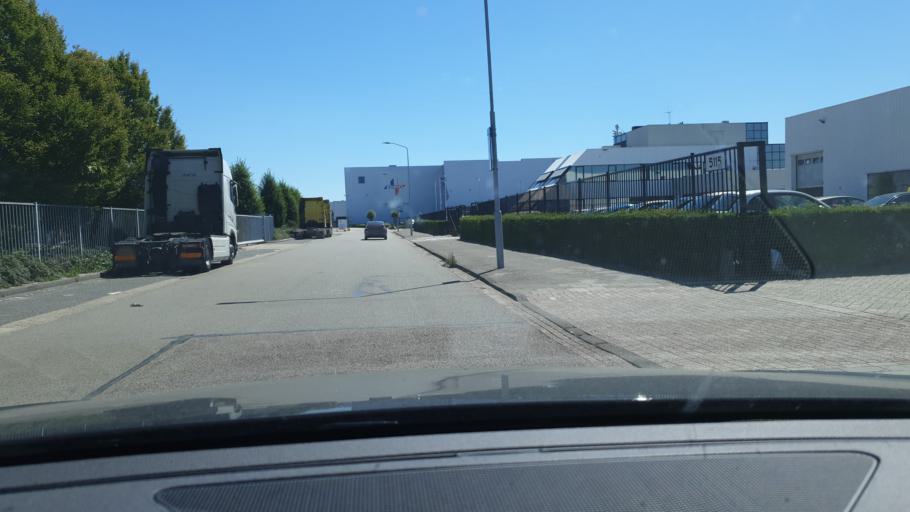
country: NL
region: North Brabant
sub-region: Gemeente Eindhoven
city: Meerhoven
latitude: 51.4535
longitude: 5.3954
